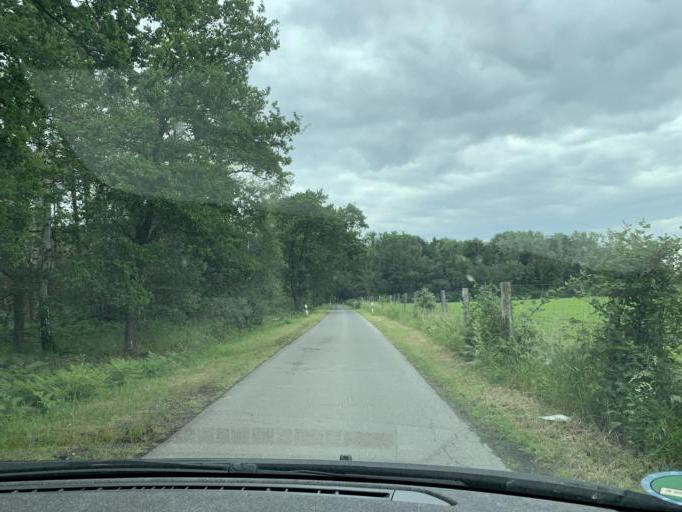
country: DE
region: North Rhine-Westphalia
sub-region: Regierungsbezirk Koln
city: Niederzier
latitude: 50.8751
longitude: 6.5139
